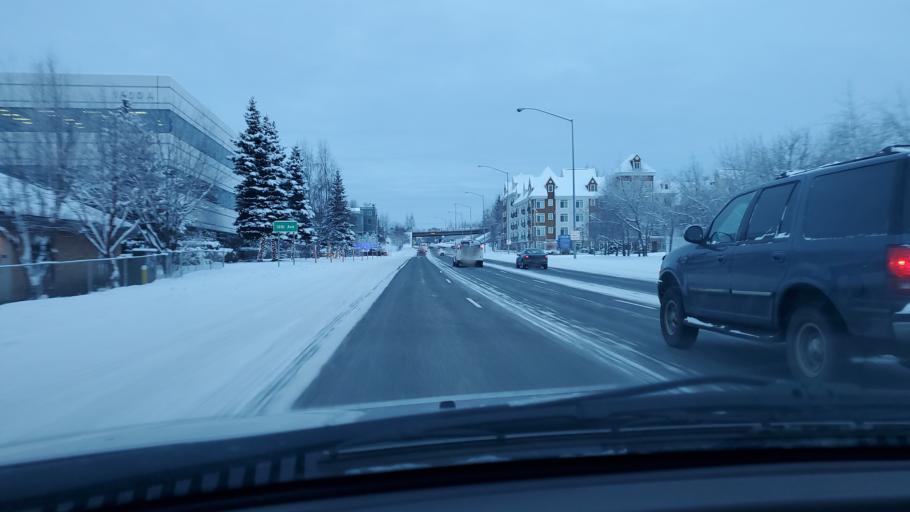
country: US
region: Alaska
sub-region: Anchorage Municipality
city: Anchorage
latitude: 61.2049
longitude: -149.8834
